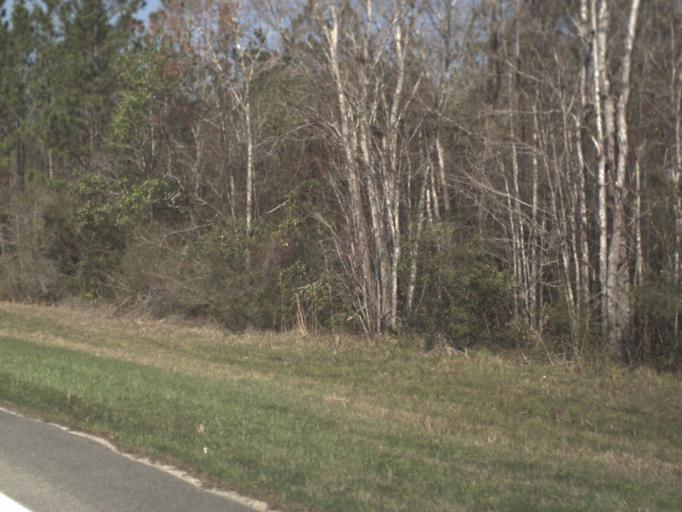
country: US
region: Florida
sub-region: Liberty County
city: Bristol
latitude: 30.3859
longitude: -84.7611
